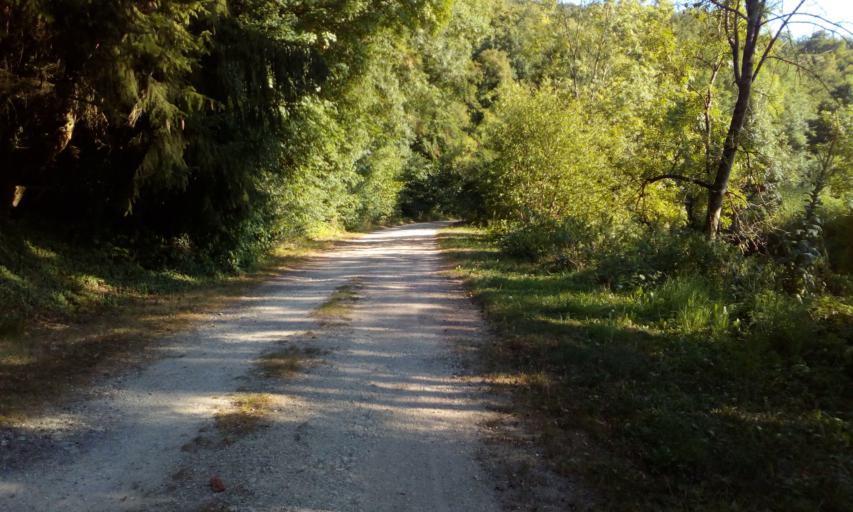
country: FR
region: Lorraine
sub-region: Departement de Meurthe-et-Moselle
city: Pagny-sur-Moselle
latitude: 48.9647
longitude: 5.8894
